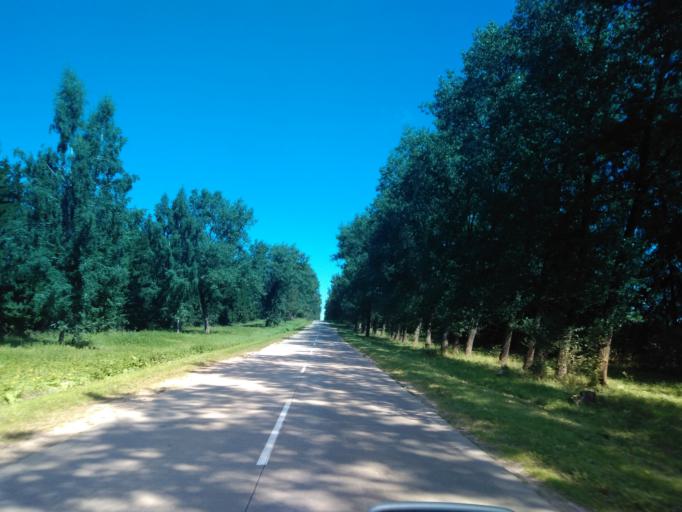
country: BY
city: Fanipol
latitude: 53.6721
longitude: 27.3464
